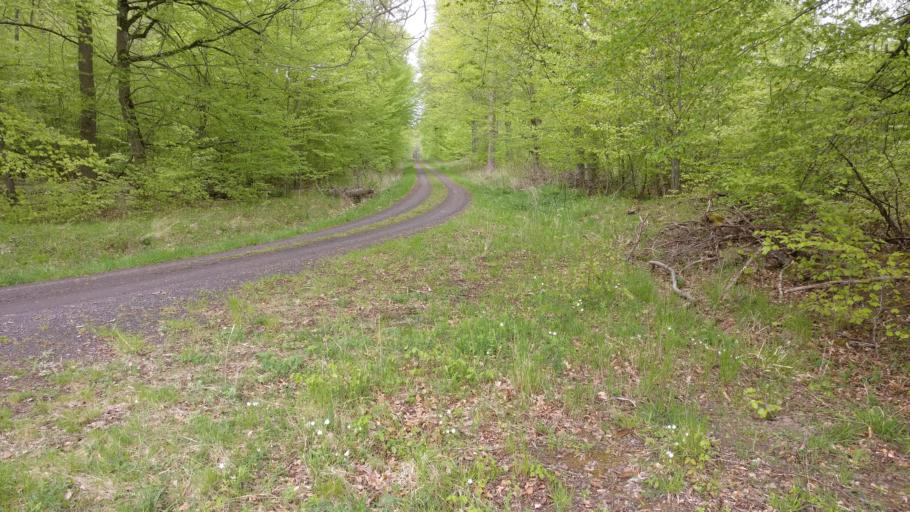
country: DE
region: Hesse
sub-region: Regierungsbezirk Giessen
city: Lautertal
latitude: 50.6484
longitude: 9.2907
